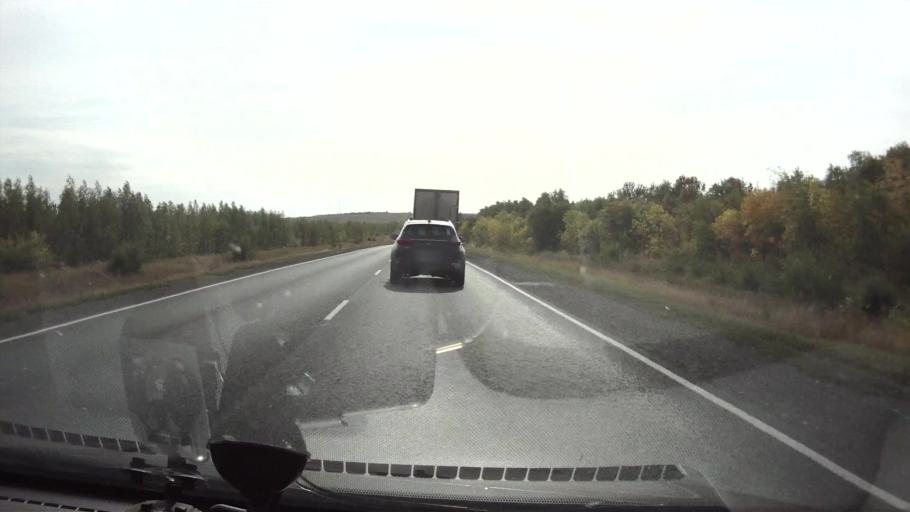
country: RU
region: Saratov
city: Balakovo
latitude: 52.1530
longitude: 47.8136
